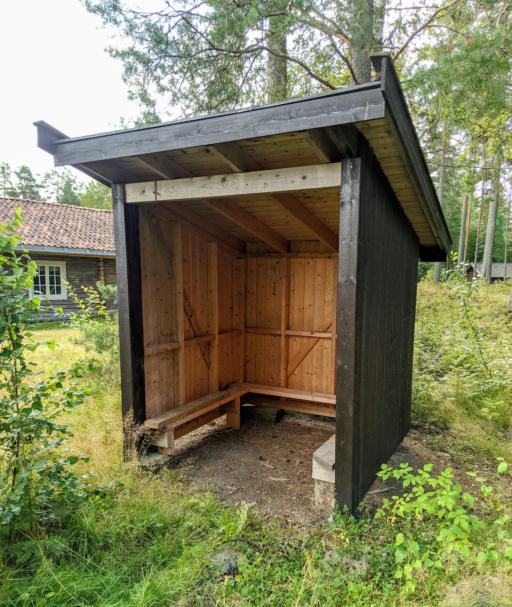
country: NO
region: Hedmark
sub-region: Sor-Odal
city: Skarnes
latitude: 60.2664
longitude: 11.6791
